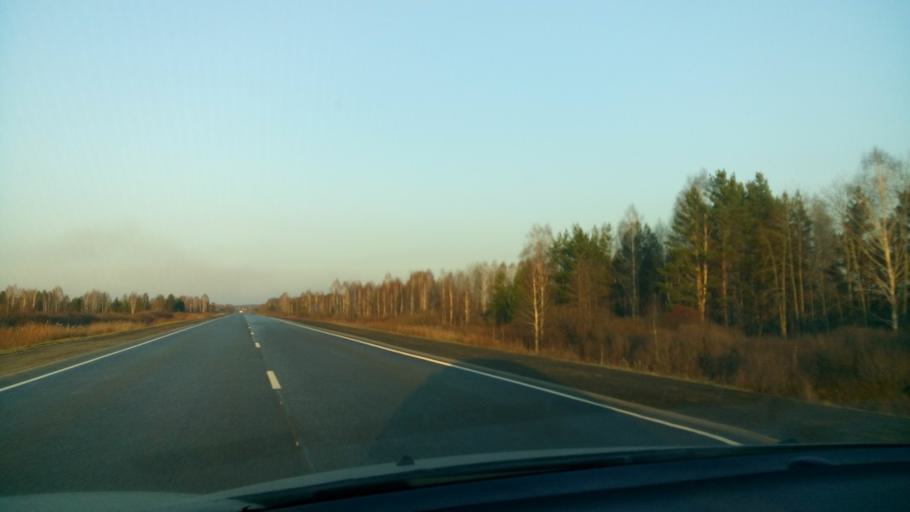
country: RU
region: Sverdlovsk
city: Yelanskiy
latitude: 56.8204
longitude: 62.5471
